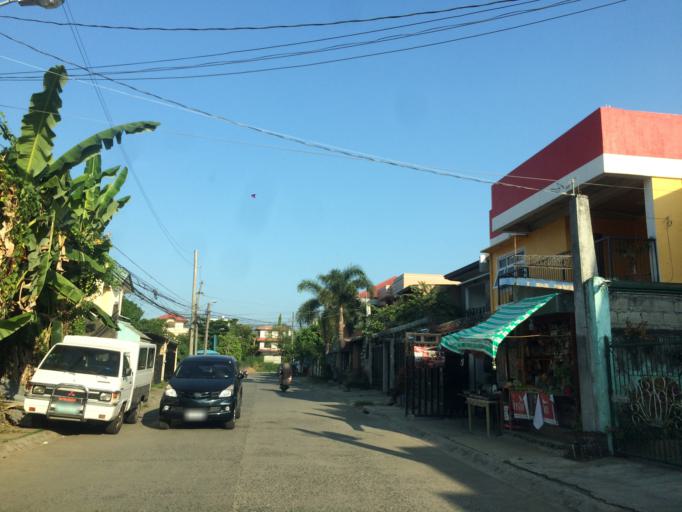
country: PH
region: Calabarzon
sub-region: Province of Rizal
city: San Mateo
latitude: 14.6755
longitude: 121.1223
